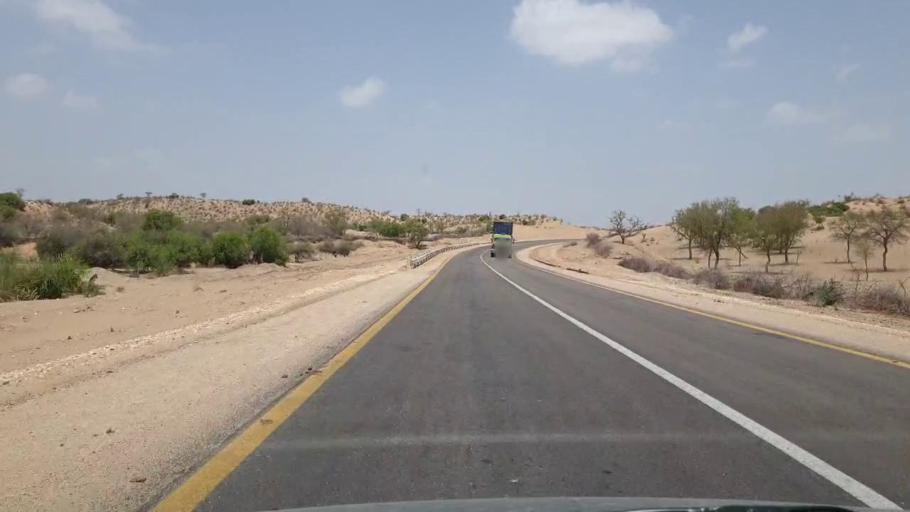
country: PK
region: Sindh
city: Mithi
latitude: 24.8076
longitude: 69.7126
